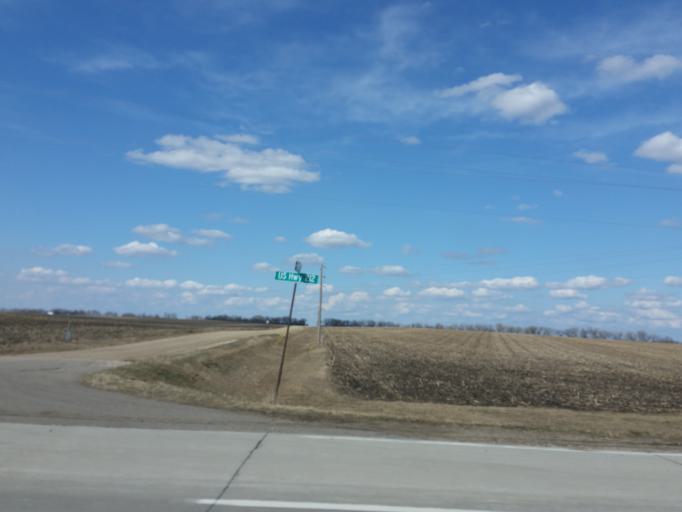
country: US
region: Minnesota
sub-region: Lac qui Parle County
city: Dawson
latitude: 44.9357
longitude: -96.0841
